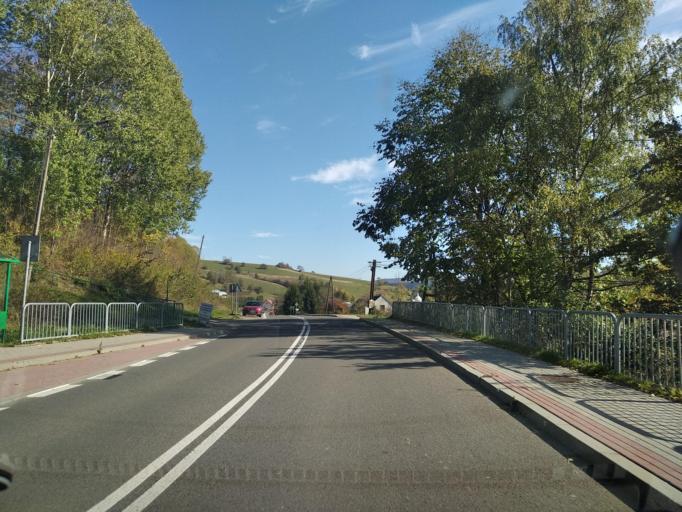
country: PL
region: Subcarpathian Voivodeship
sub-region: Powiat sanocki
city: Komancza
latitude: 49.3396
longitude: 22.0557
